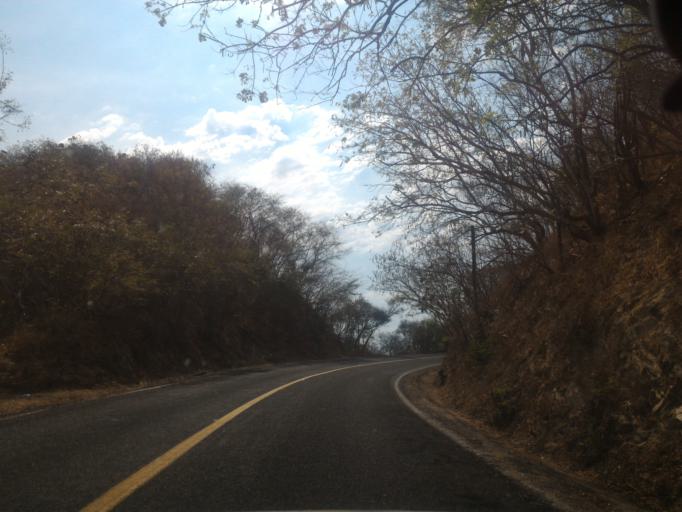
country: MX
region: Michoacan
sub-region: Coalcoman de Vazquez Pallares
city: Coalcoman de Vazquez Pallares
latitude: 18.2811
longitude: -103.3740
